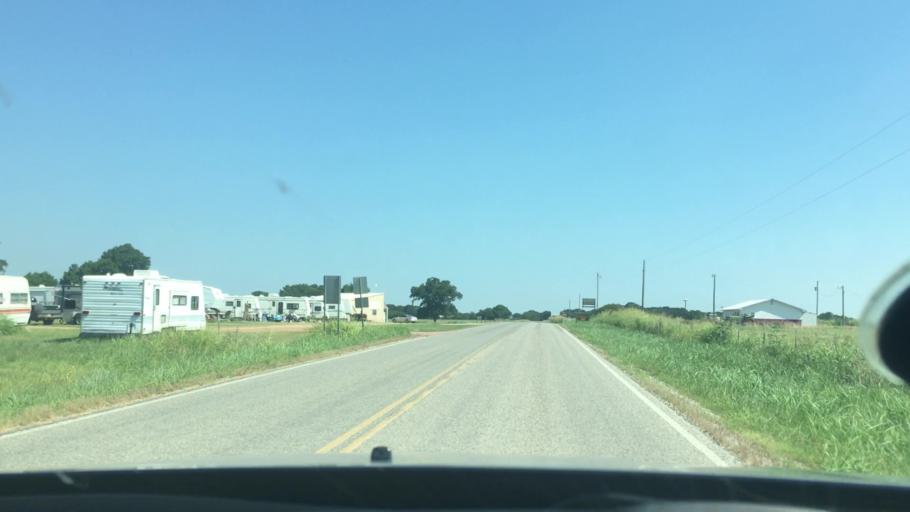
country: US
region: Oklahoma
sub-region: Johnston County
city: Tishomingo
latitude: 34.3086
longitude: -96.6184
